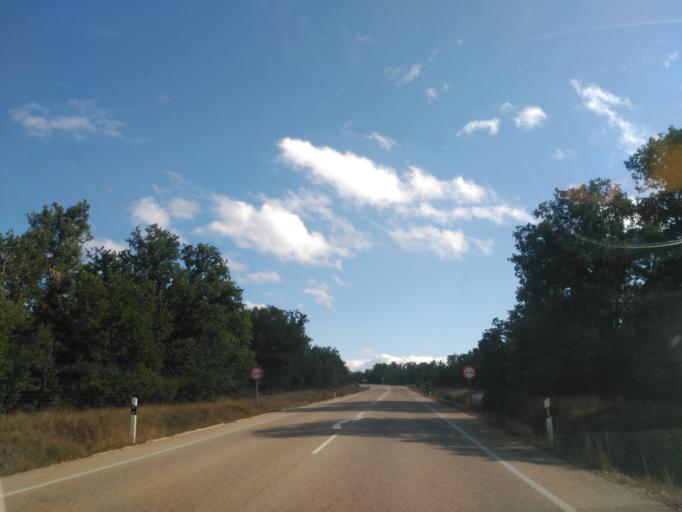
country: ES
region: Castille and Leon
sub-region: Provincia de Burgos
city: Pinilla de los Barruecos
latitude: 41.9308
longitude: -3.2827
